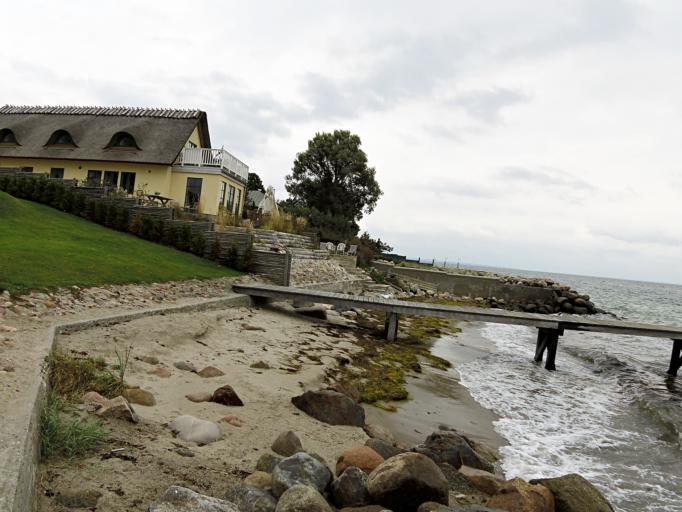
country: DK
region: Capital Region
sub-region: Rudersdal Kommune
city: Trorod
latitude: 55.8538
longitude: 12.5684
